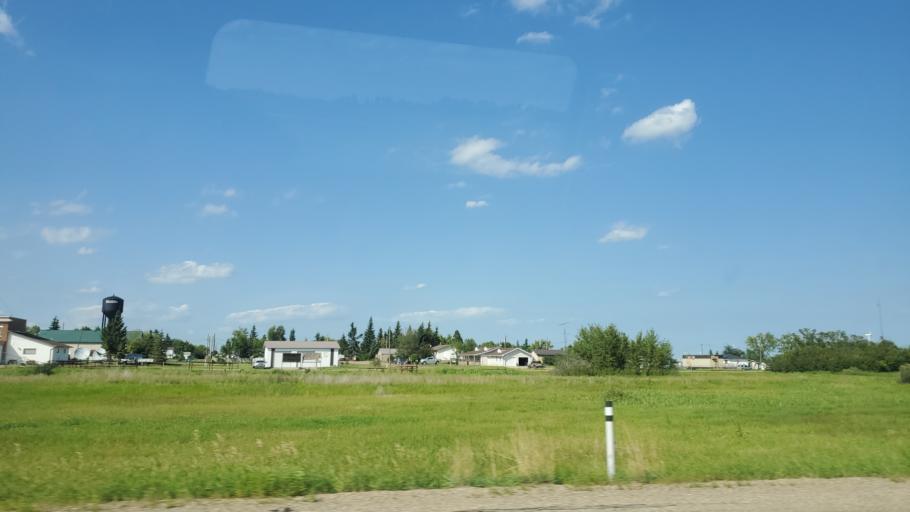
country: CA
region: Alberta
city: Stettler
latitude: 52.2805
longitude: -112.1533
